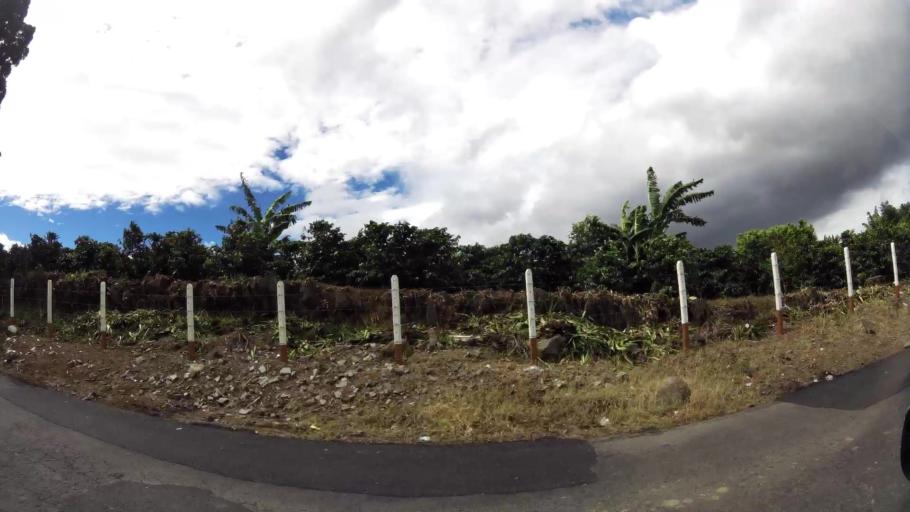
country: CR
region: Cartago
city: Tres Rios
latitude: 9.9201
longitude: -83.9928
